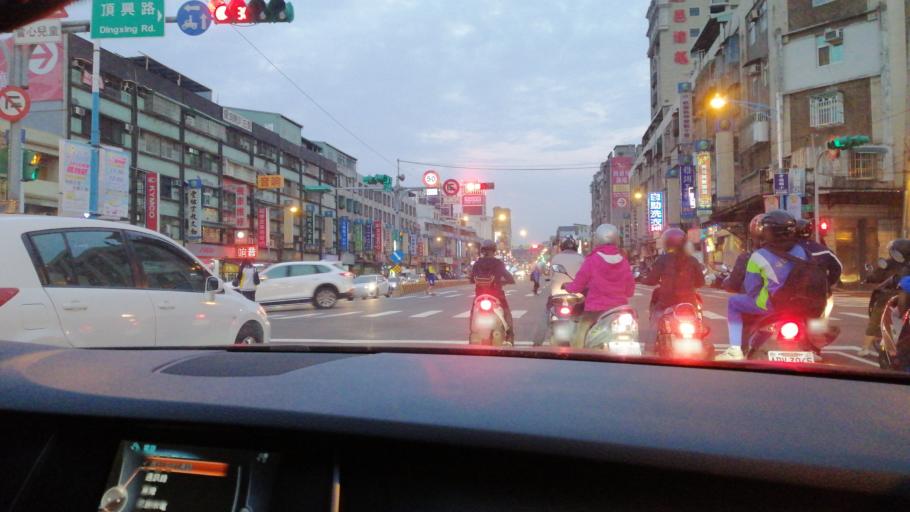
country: TW
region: Taiwan
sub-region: Taoyuan
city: Taoyuan
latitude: 24.9929
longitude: 121.3273
